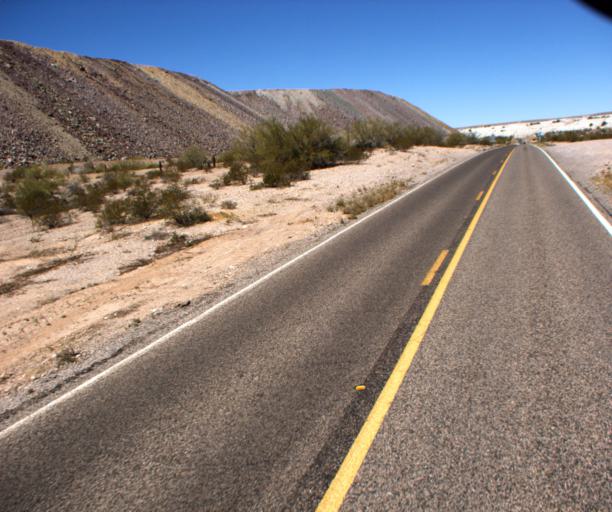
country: US
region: Arizona
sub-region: Pima County
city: Ajo
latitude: 32.3613
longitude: -112.8338
